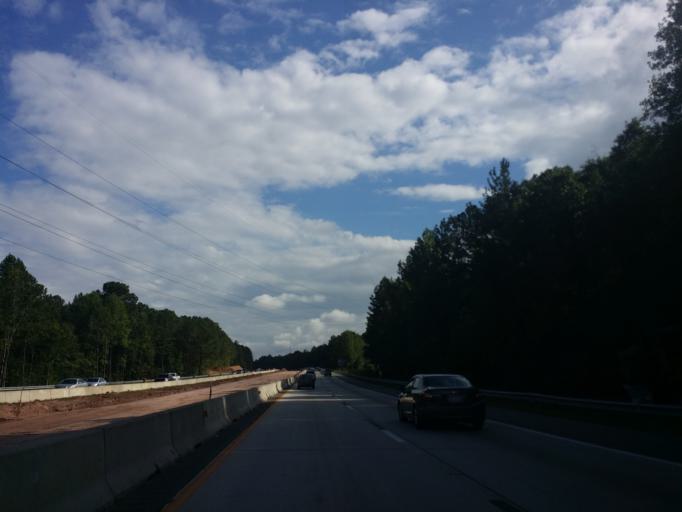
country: US
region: North Carolina
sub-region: Durham County
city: Durham
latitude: 35.9553
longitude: -78.8642
